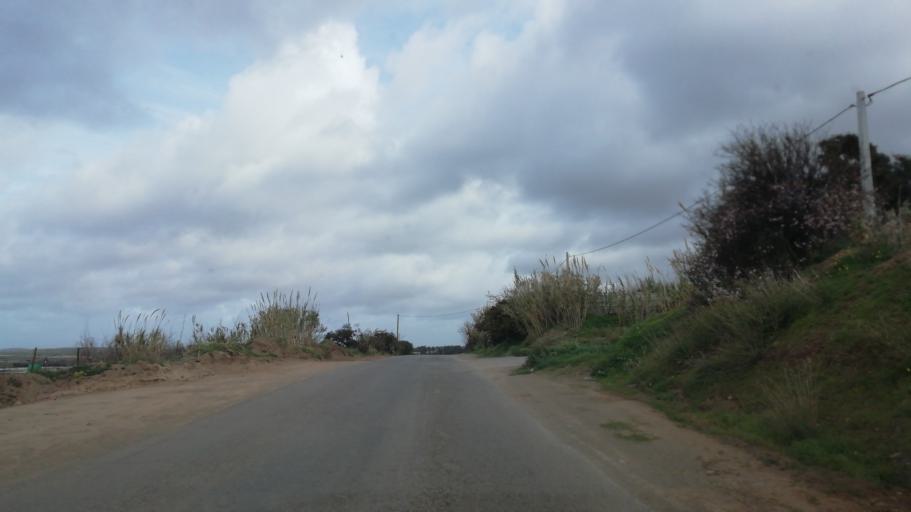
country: DZ
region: Oran
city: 'Ain el Turk
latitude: 35.6990
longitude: -0.8496
